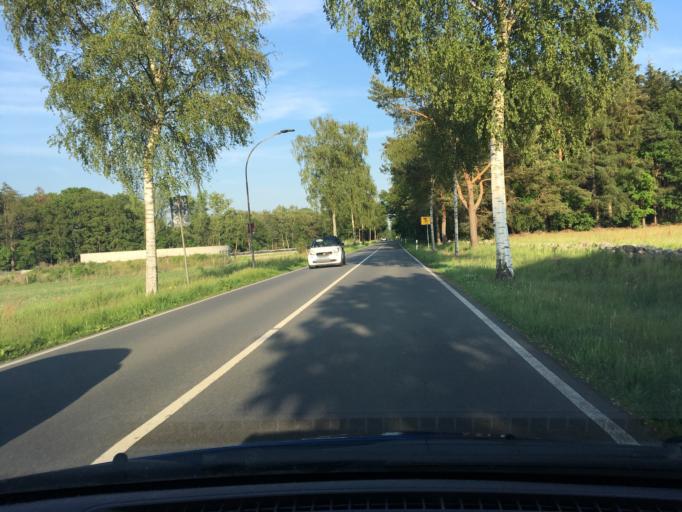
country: DE
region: Lower Saxony
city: Welle
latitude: 53.2469
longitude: 9.7854
